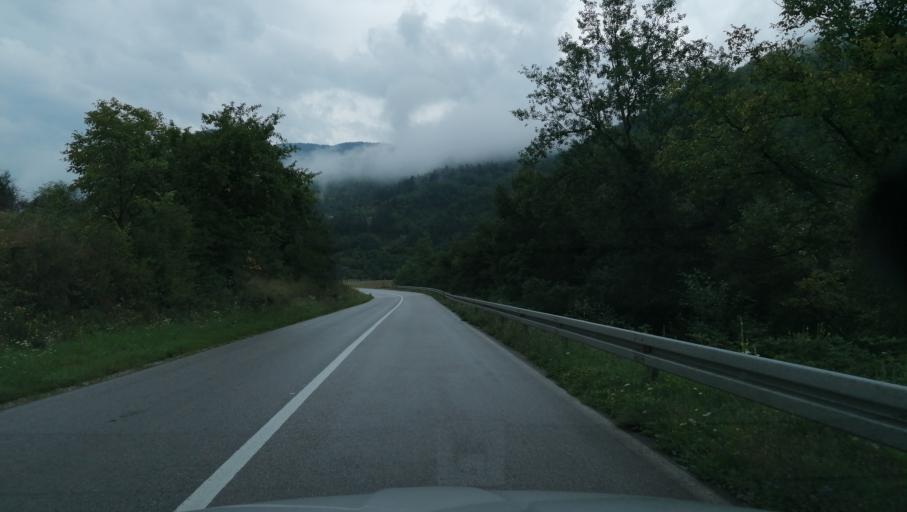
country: RS
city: Durici
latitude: 43.7625
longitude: 19.3865
